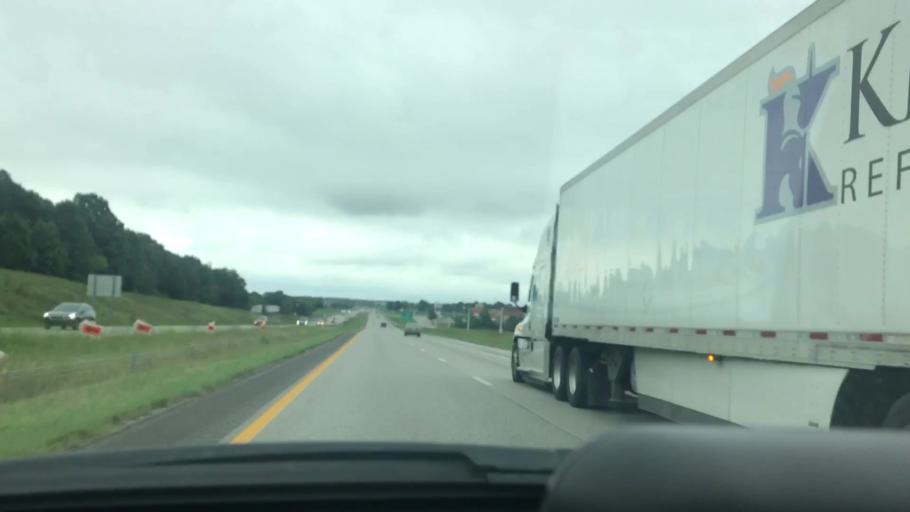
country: US
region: Missouri
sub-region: Jasper County
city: Joplin
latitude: 37.0457
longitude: -94.4922
